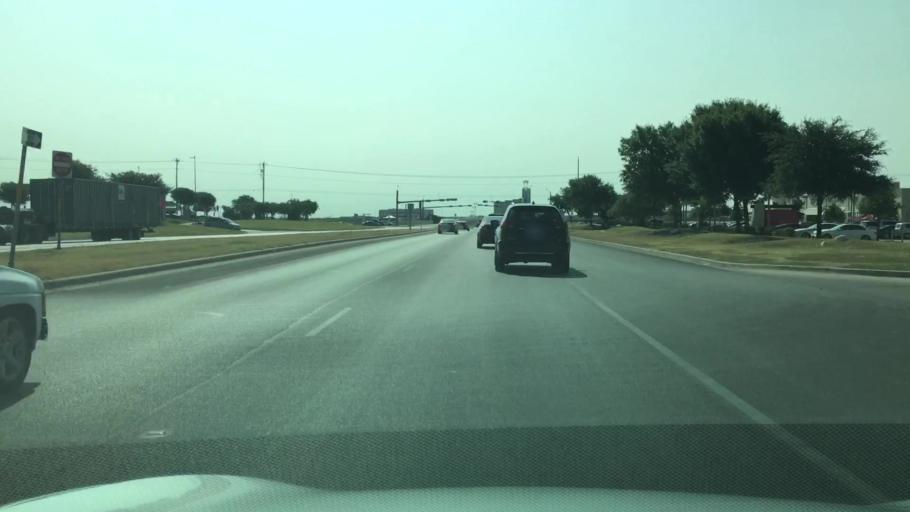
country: US
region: Texas
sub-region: Hays County
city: Kyle
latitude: 30.0141
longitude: -97.8636
